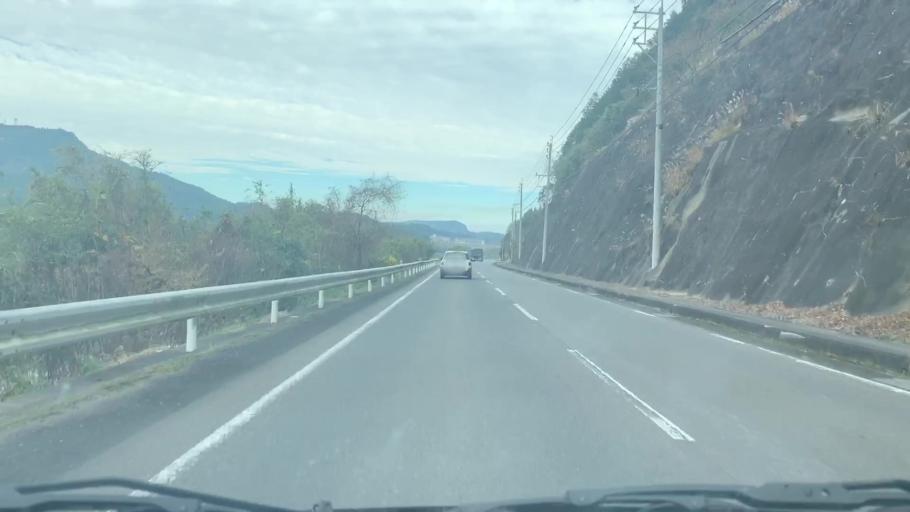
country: JP
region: Saga Prefecture
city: Imaricho-ko
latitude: 33.2725
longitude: 129.9647
